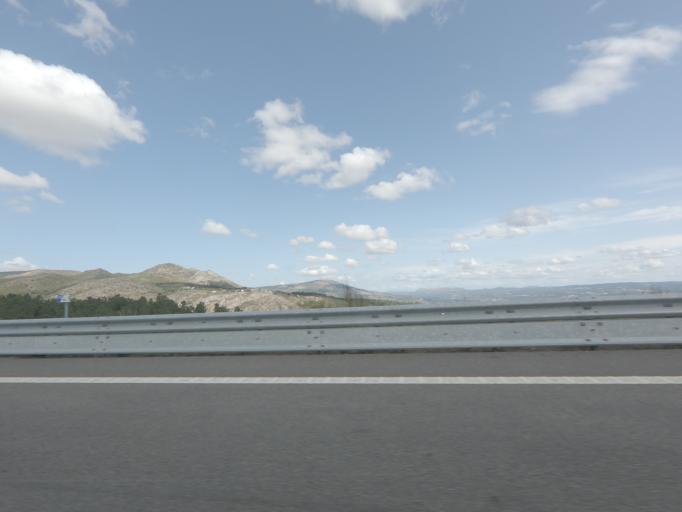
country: PT
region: Vila Real
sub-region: Santa Marta de Penaguiao
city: Santa Marta de Penaguiao
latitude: 41.2764
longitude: -7.8205
